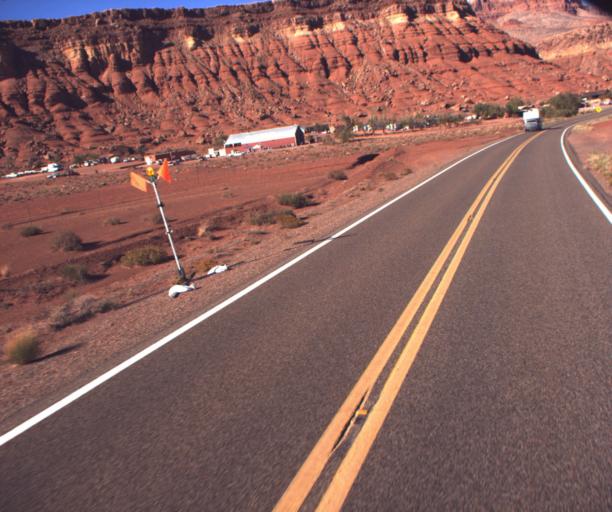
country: US
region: Arizona
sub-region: Coconino County
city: Page
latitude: 36.7404
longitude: -111.7545
